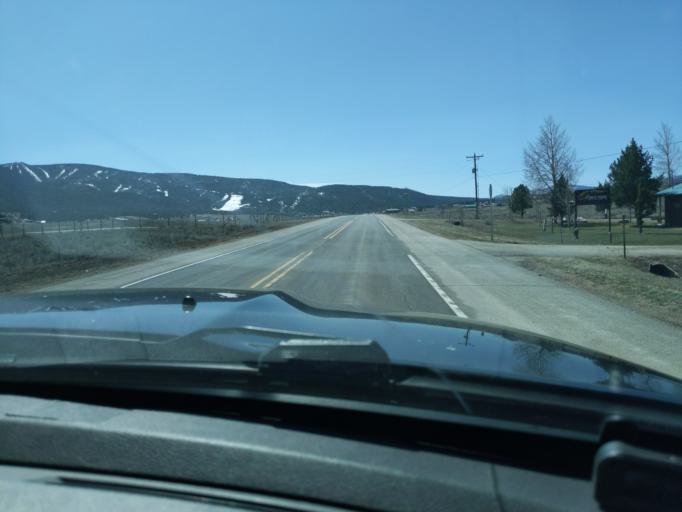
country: US
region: New Mexico
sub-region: Colfax County
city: Angel Fire
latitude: 36.4128
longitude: -105.2936
